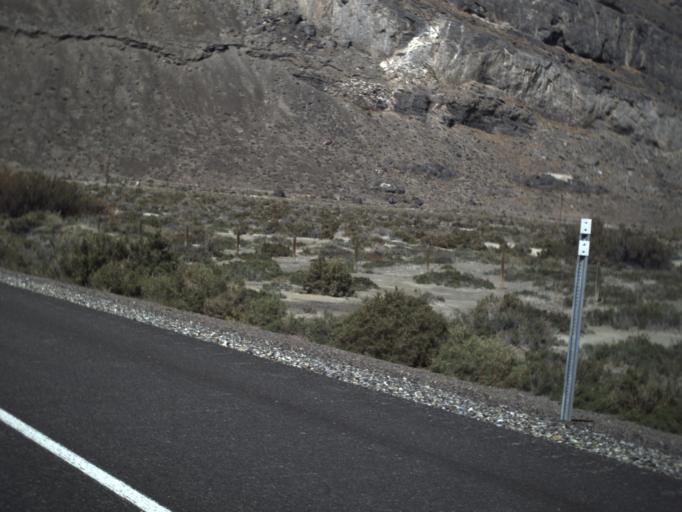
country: US
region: Utah
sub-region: Tooele County
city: Wendover
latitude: 40.7493
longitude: -114.0114
